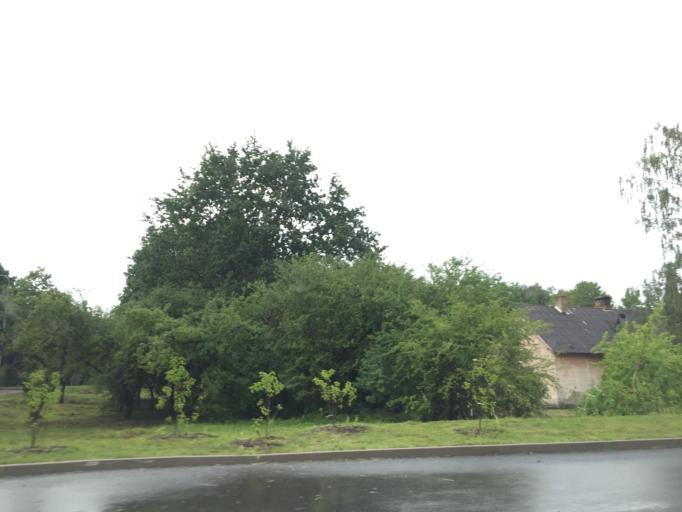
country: LV
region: Dobeles Rajons
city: Dobele
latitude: 56.6258
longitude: 23.2855
